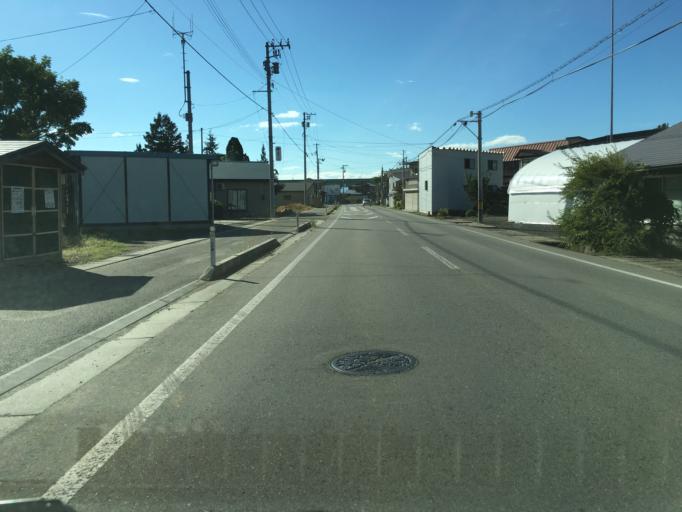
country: JP
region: Yamagata
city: Takahata
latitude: 37.9848
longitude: 140.1568
